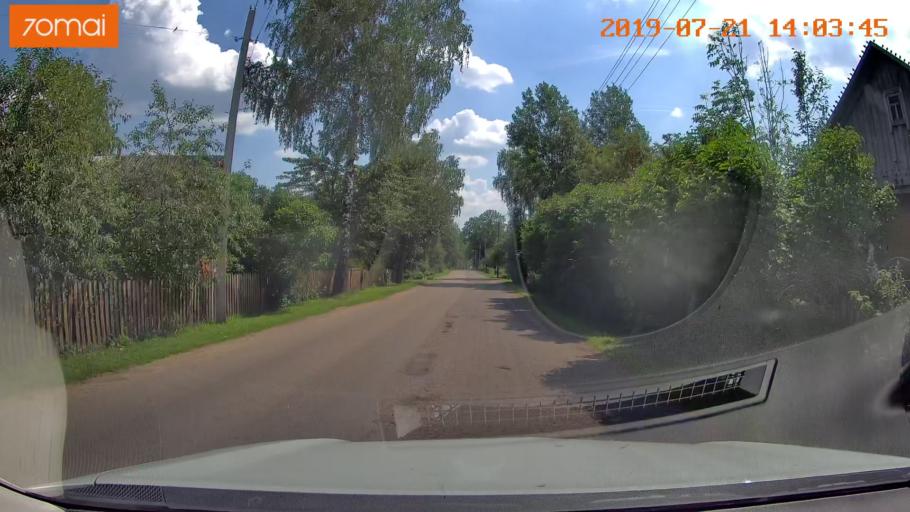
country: BY
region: Grodnenskaya
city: Lyubcha
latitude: 53.7265
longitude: 26.0935
